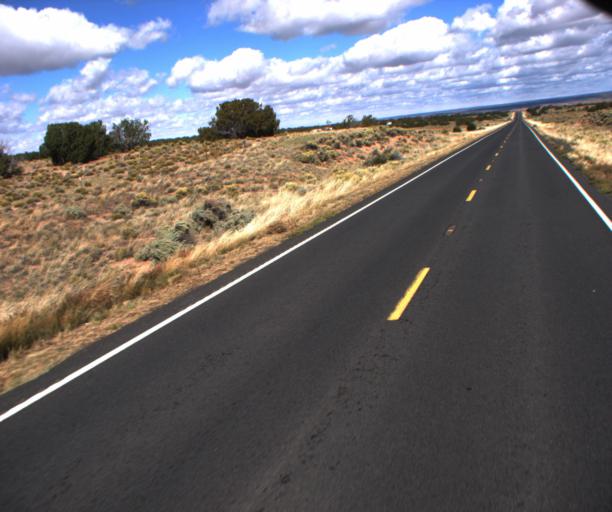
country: US
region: Arizona
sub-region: Apache County
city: Houck
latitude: 35.1351
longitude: -109.3312
